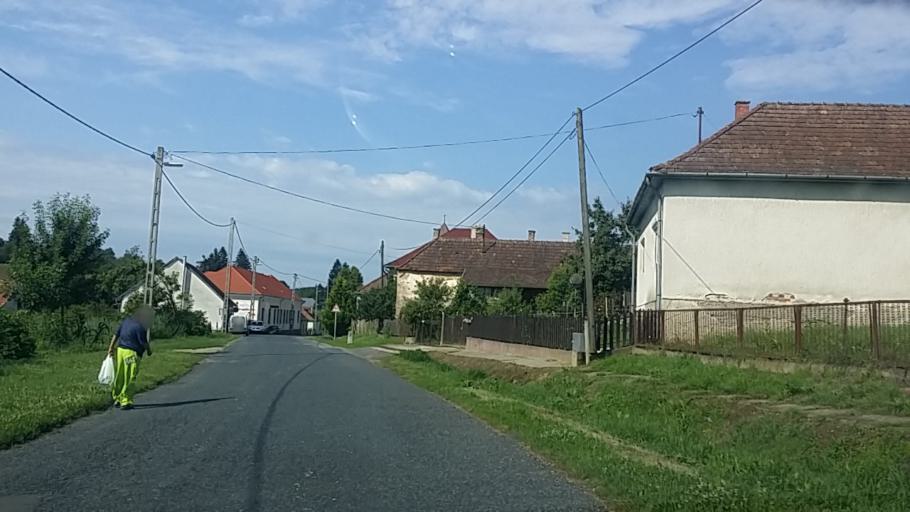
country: HU
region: Zala
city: Letenye
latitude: 46.5415
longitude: 16.6955
